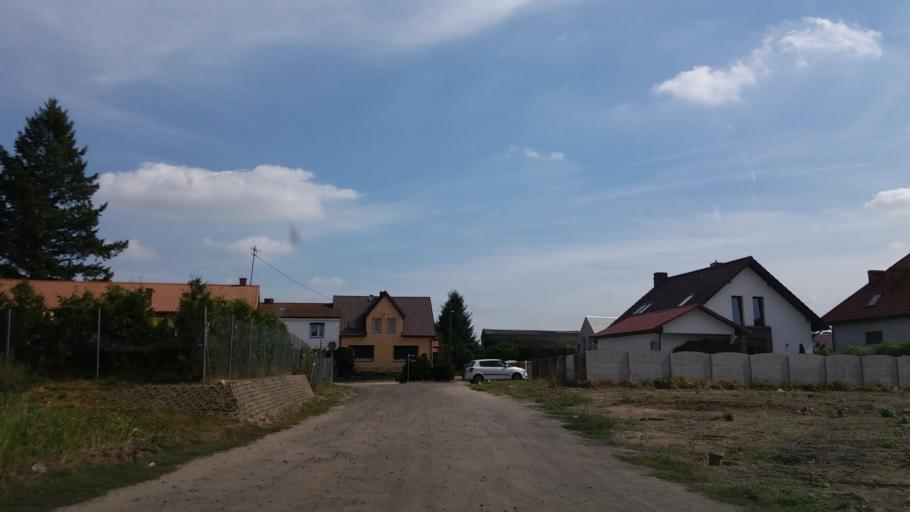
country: PL
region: West Pomeranian Voivodeship
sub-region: Powiat stargardzki
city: Stargard Szczecinski
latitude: 53.3682
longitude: 14.9715
